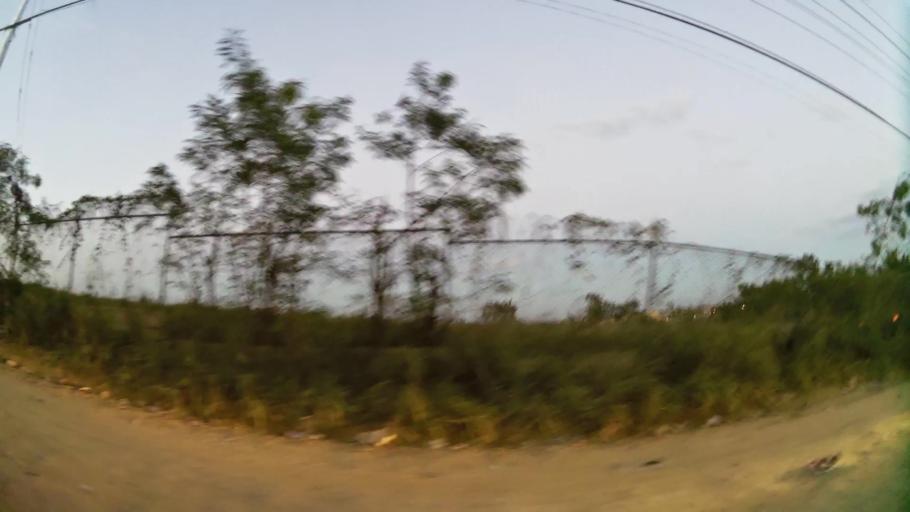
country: DO
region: Nacional
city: La Agustina
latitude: 18.5462
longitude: -69.9399
